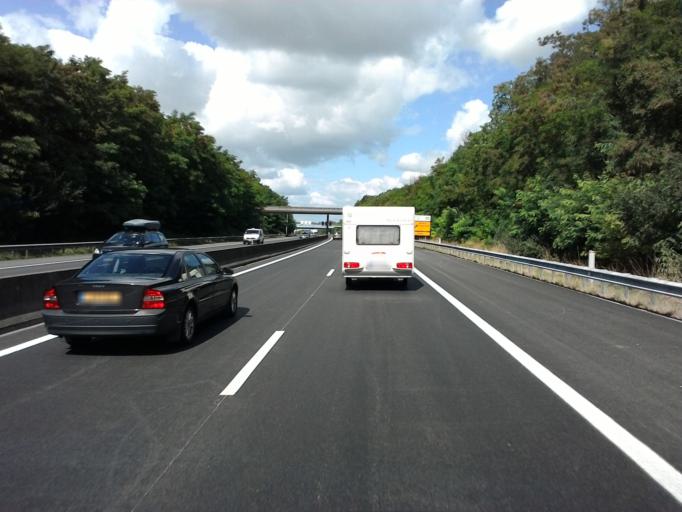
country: LU
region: Luxembourg
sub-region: Canton de Capellen
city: Mamer
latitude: 49.6374
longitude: 6.0226
